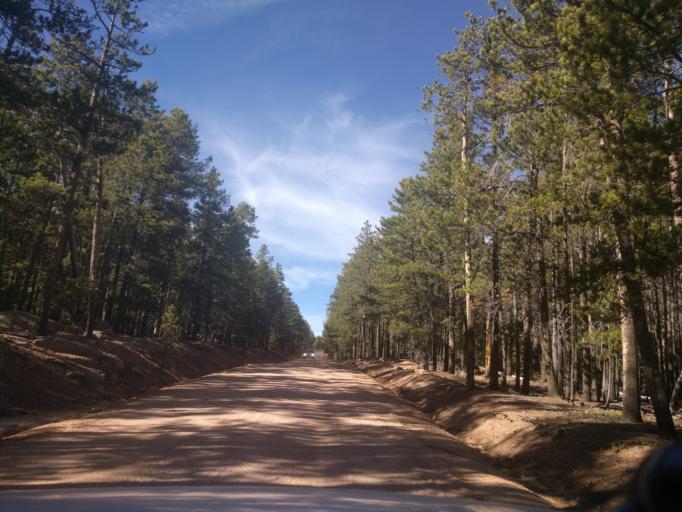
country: US
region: Colorado
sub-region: Douglas County
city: Perry Park
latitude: 39.1878
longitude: -105.0479
